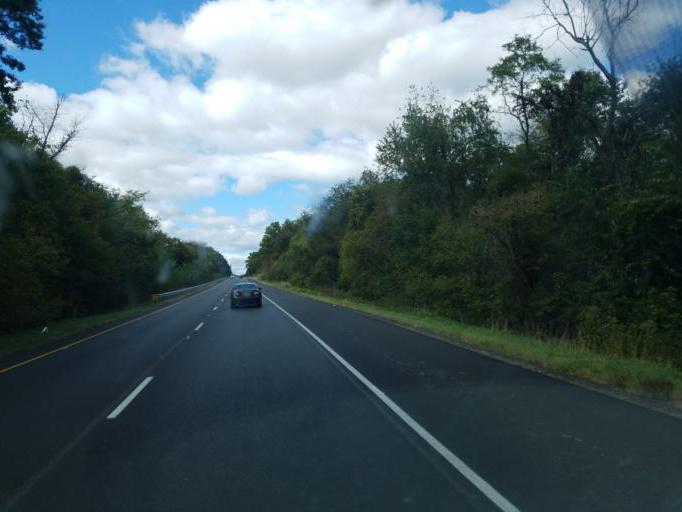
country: US
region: Maryland
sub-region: Washington County
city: Wilson-Conococheague
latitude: 39.6465
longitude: -77.8376
